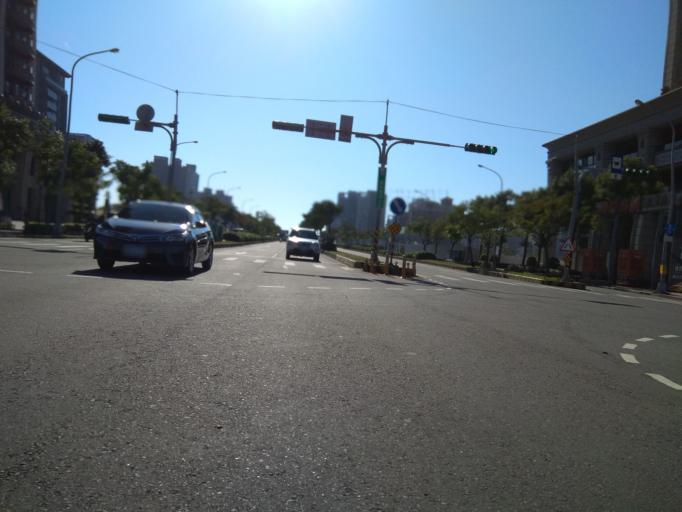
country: TW
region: Taiwan
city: Taoyuan City
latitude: 25.0087
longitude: 121.2184
